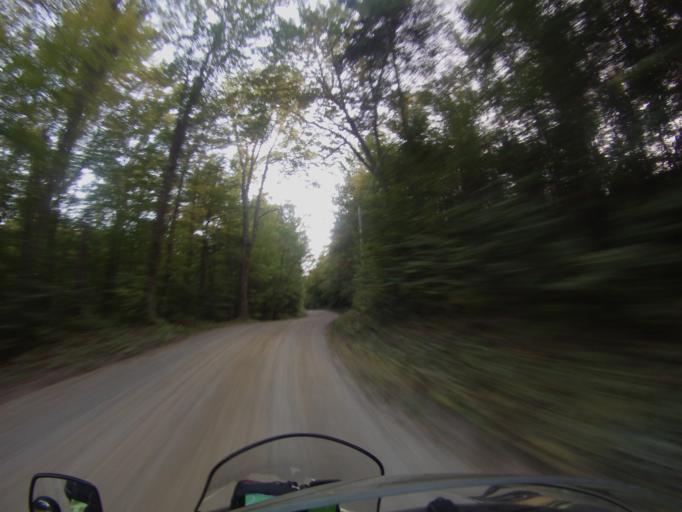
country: US
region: Vermont
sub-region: Addison County
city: Bristol
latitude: 44.0173
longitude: -73.0262
